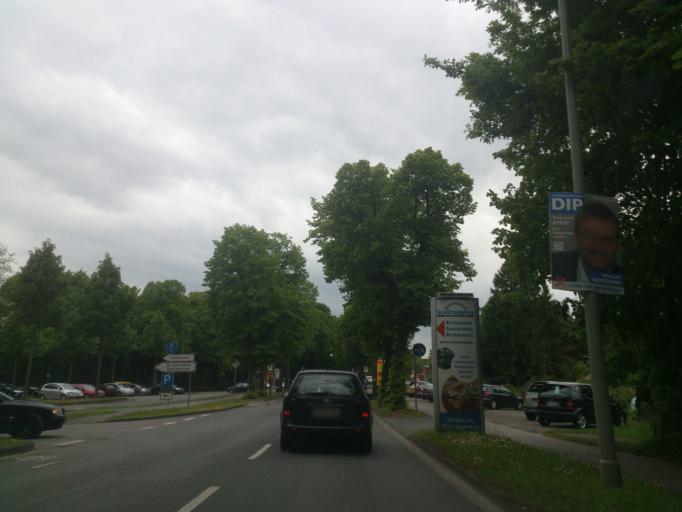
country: DE
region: North Rhine-Westphalia
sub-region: Regierungsbezirk Detmold
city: Paderborn
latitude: 51.7317
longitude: 8.7517
